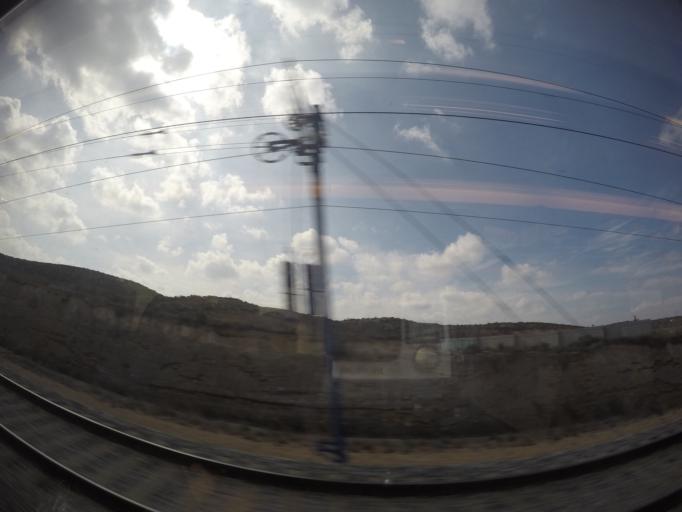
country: ES
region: Aragon
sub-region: Provincia de Zaragoza
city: El Burgo de Ebro
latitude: 41.5576
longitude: -0.7658
